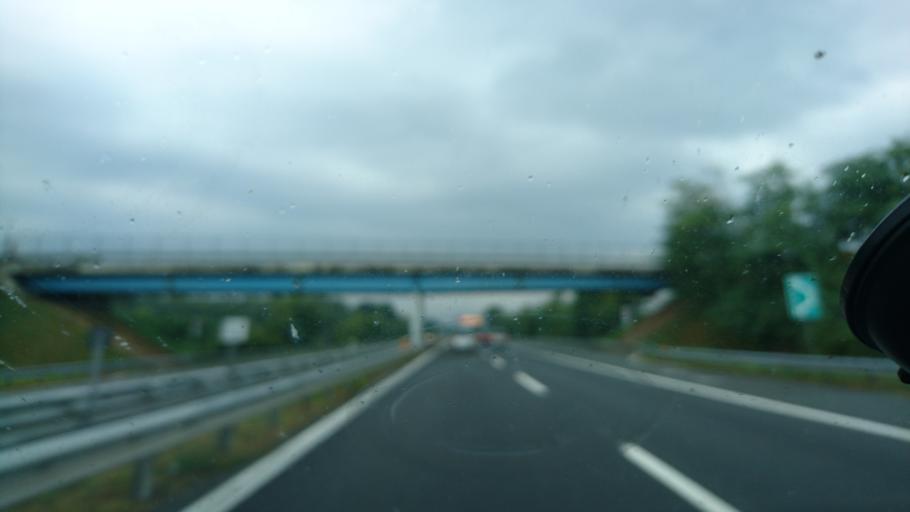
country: IT
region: Piedmont
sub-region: Provincia di Novara
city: Ghemme
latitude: 45.5885
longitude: 8.4040
